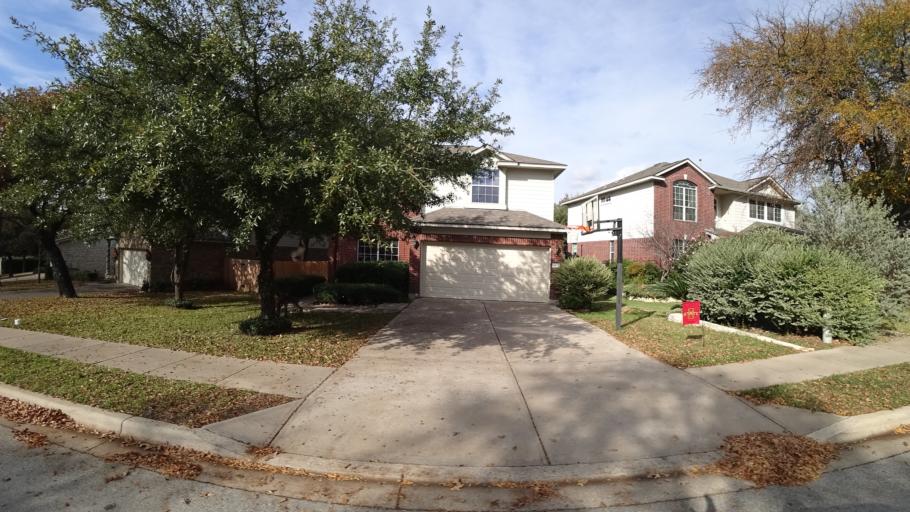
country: US
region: Texas
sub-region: Williamson County
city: Brushy Creek
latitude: 30.5055
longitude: -97.7469
